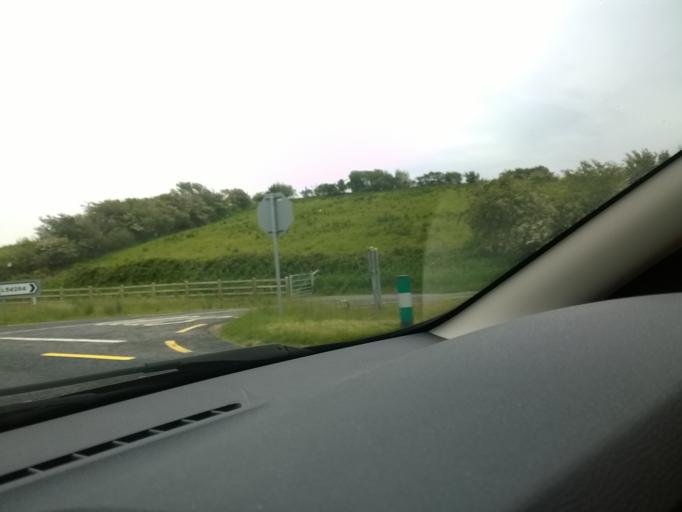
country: IE
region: Connaught
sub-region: Maigh Eo
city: Westport
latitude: 53.8771
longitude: -9.5458
